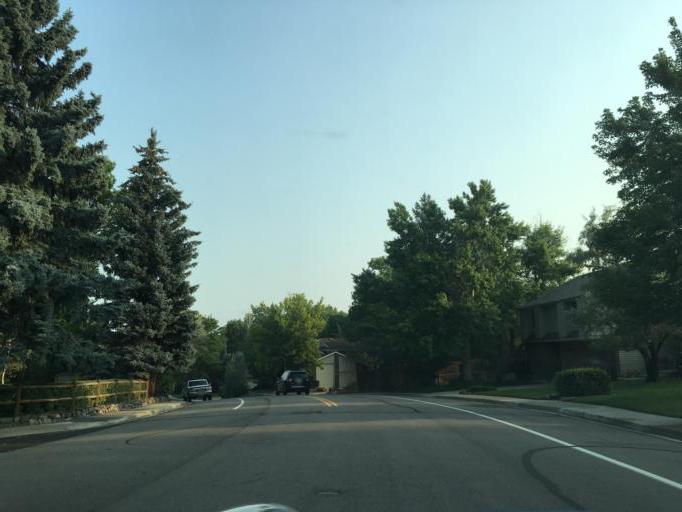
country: US
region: Colorado
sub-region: Adams County
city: Westminster
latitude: 39.8803
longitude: -105.0471
